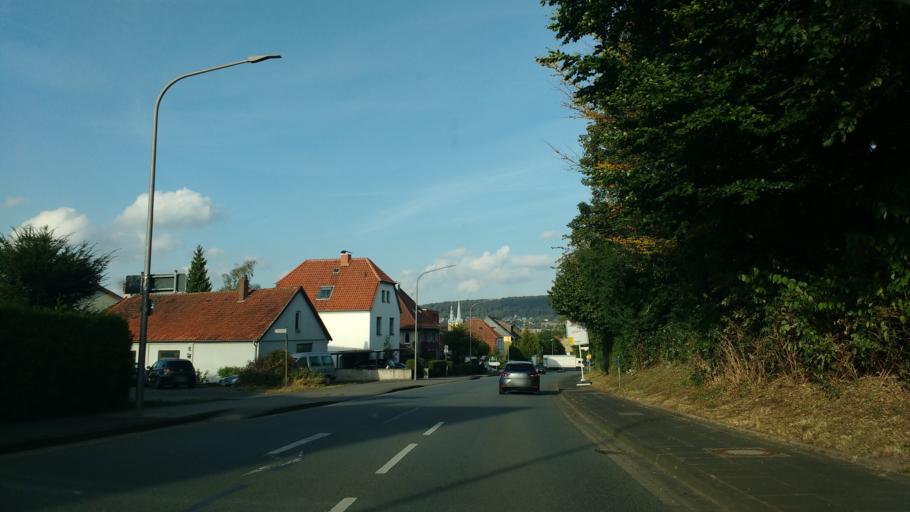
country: DE
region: North Rhine-Westphalia
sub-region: Regierungsbezirk Detmold
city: Lemgo
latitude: 52.0209
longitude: 8.8948
